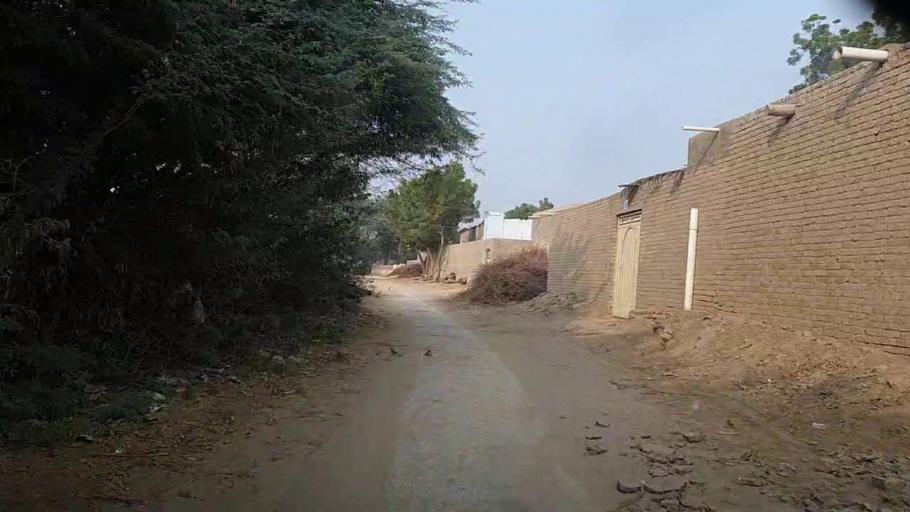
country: PK
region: Sindh
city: Bozdar
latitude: 27.1367
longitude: 68.6617
